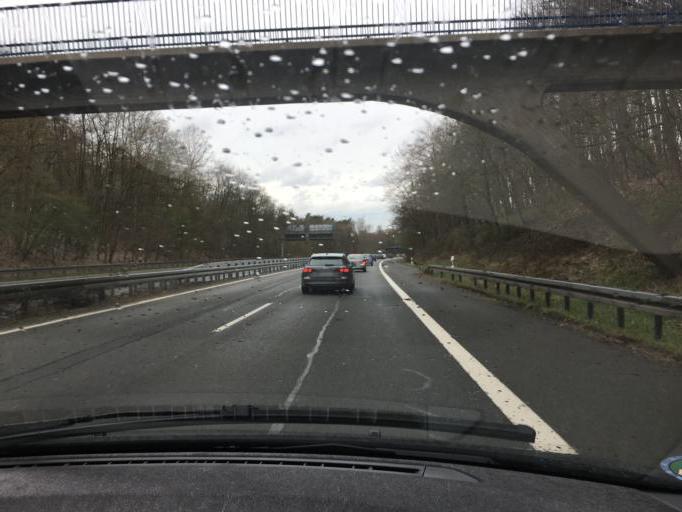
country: DE
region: North Rhine-Westphalia
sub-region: Regierungsbezirk Arnsberg
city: Dortmund
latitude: 51.4522
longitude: 7.4849
